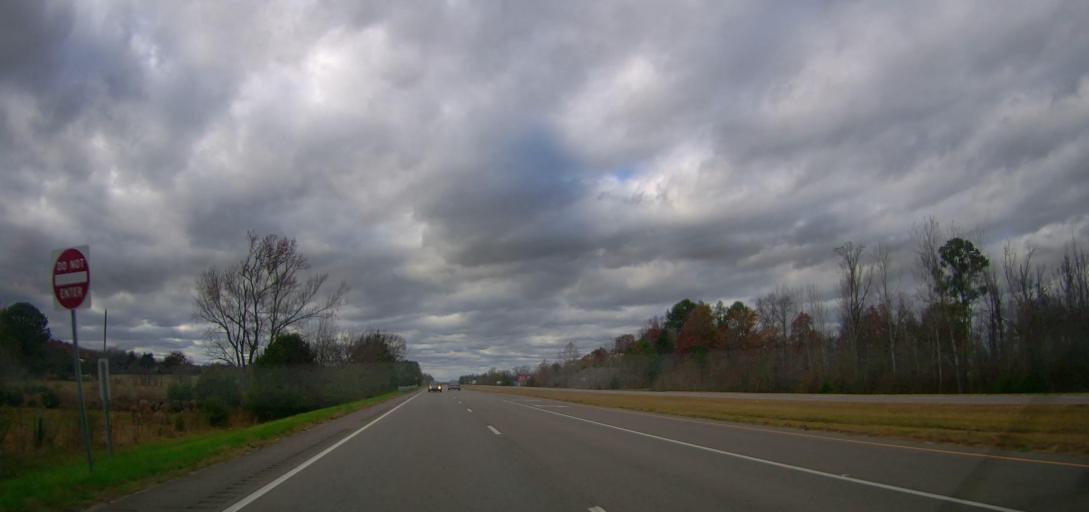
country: US
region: Alabama
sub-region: Morgan County
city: Falkville
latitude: 34.3327
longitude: -87.0125
